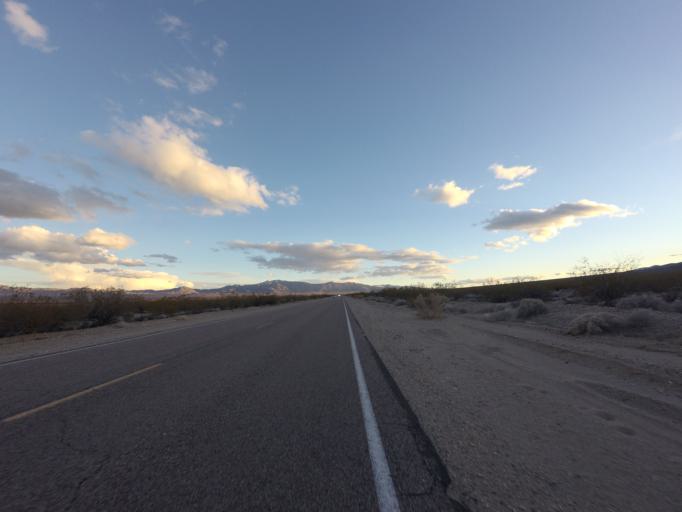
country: US
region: Nevada
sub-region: Clark County
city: Sandy Valley
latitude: 35.4401
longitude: -115.3874
